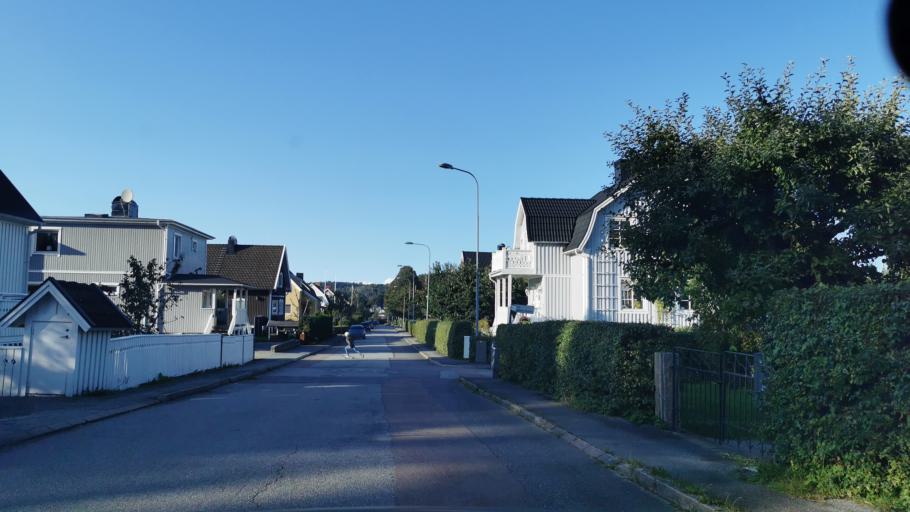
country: SE
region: Vaestra Goetaland
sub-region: Goteborg
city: Eriksbo
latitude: 57.7279
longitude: 12.0594
